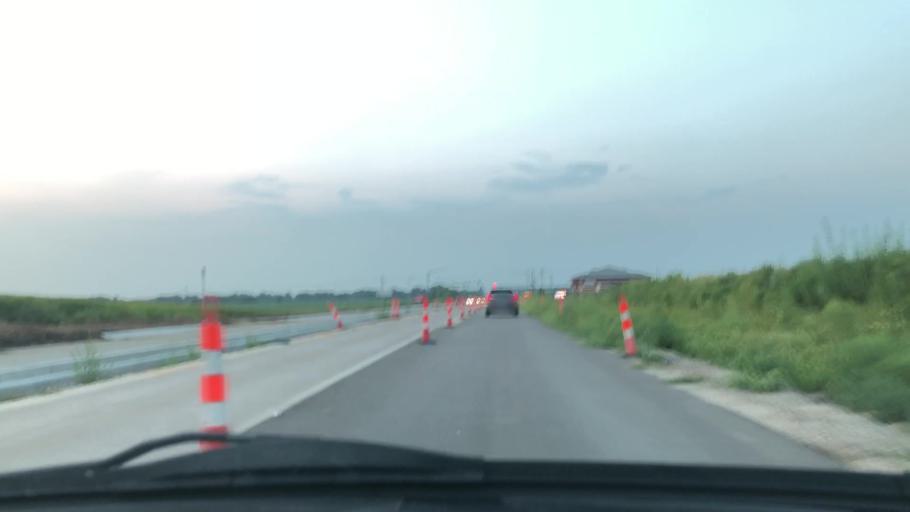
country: US
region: Iowa
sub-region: Johnson County
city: North Liberty
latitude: 41.7203
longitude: -91.6078
